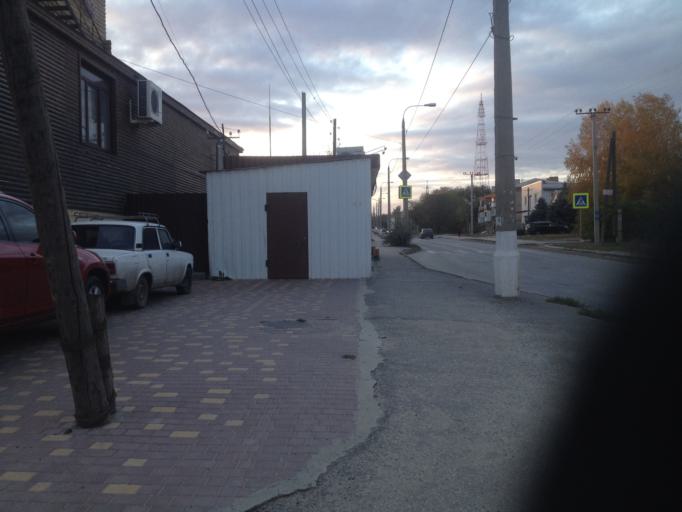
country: RU
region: Volgograd
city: Volgograd
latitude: 48.7375
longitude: 44.5144
